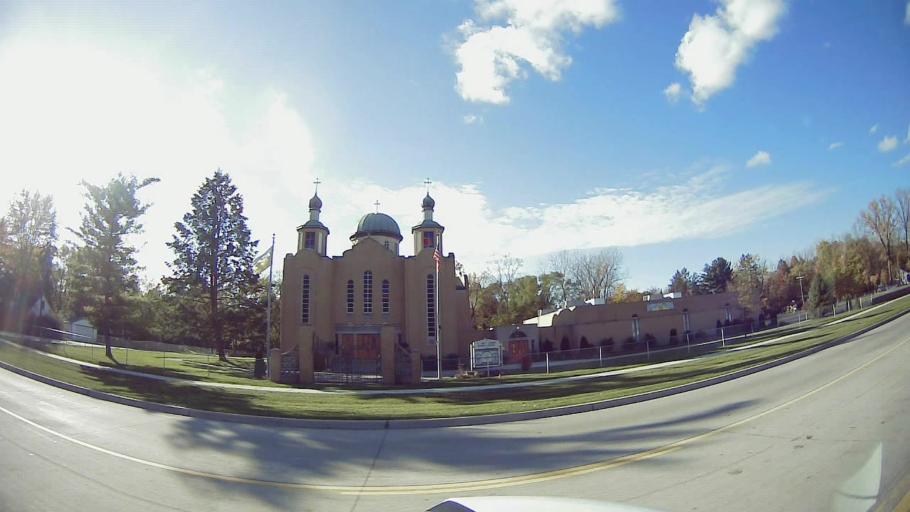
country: US
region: Michigan
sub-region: Oakland County
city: Southfield
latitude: 42.4535
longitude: -83.2400
